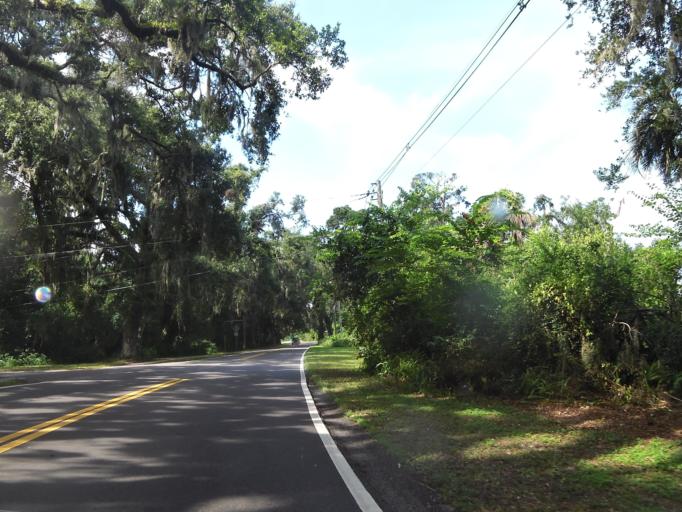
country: US
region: Florida
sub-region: Nassau County
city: Fernandina Beach
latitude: 30.5978
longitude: -81.4598
